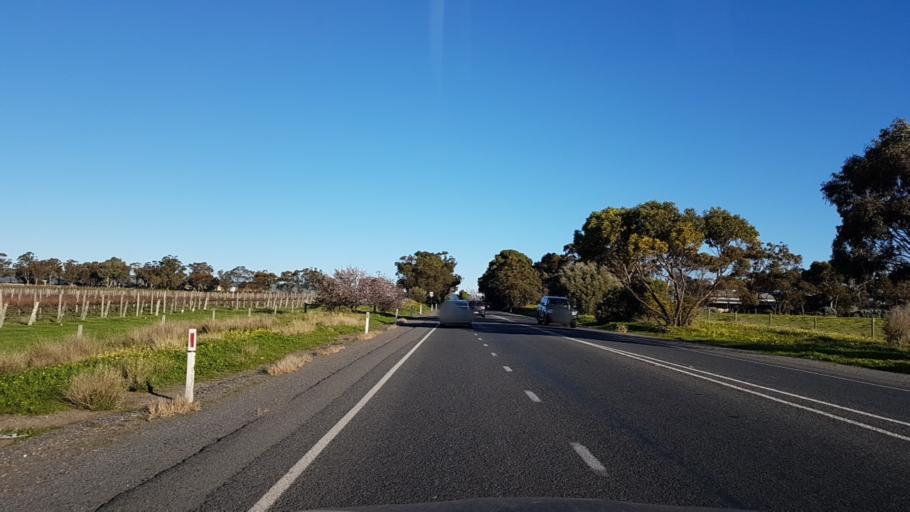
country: AU
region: South Australia
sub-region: Onkaparinga
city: Moana
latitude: -35.2346
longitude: 138.4935
